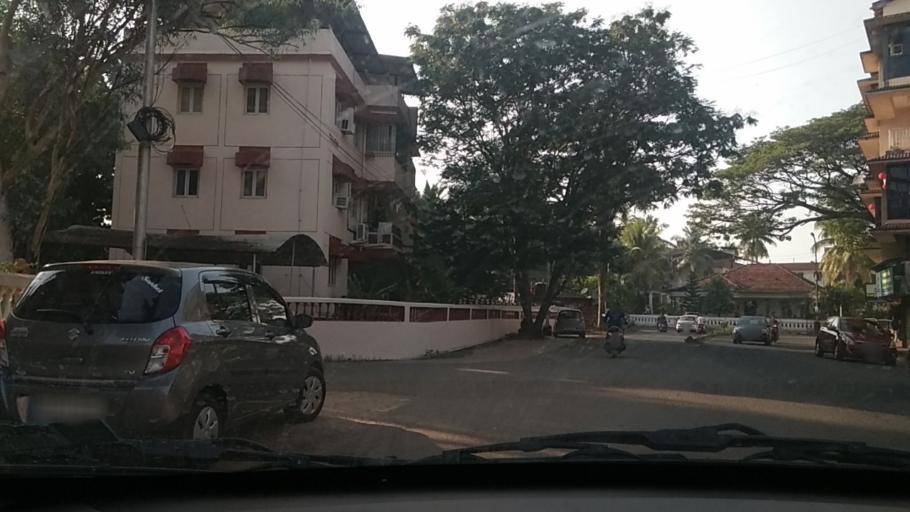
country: IN
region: Goa
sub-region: North Goa
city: Panaji
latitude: 15.4805
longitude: 73.8131
